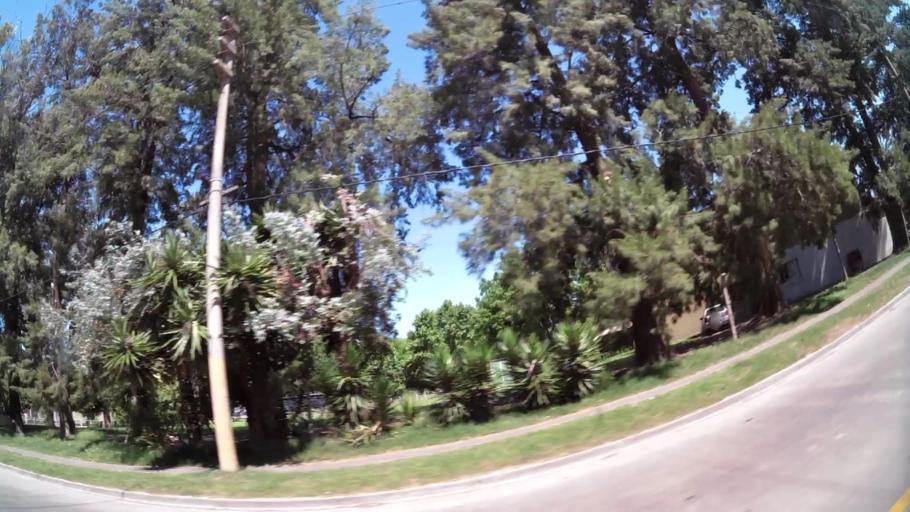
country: AR
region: Buenos Aires
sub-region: Partido de Tigre
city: Tigre
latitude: -34.4878
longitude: -58.6466
